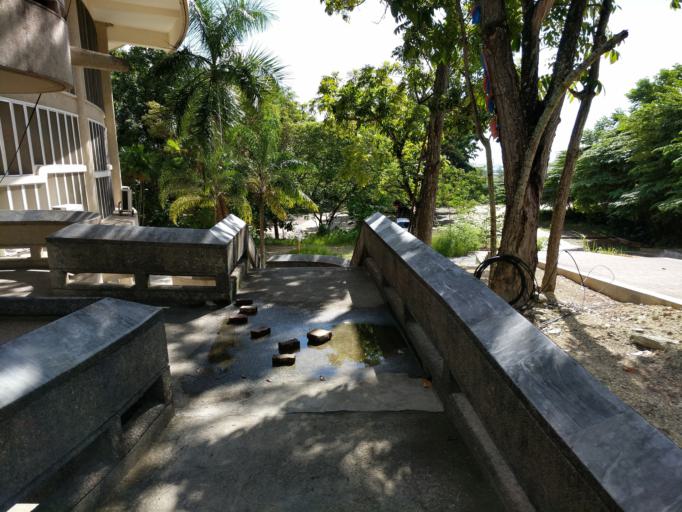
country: PH
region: Central Visayas
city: Mandaue City
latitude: 10.3528
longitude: 123.9114
